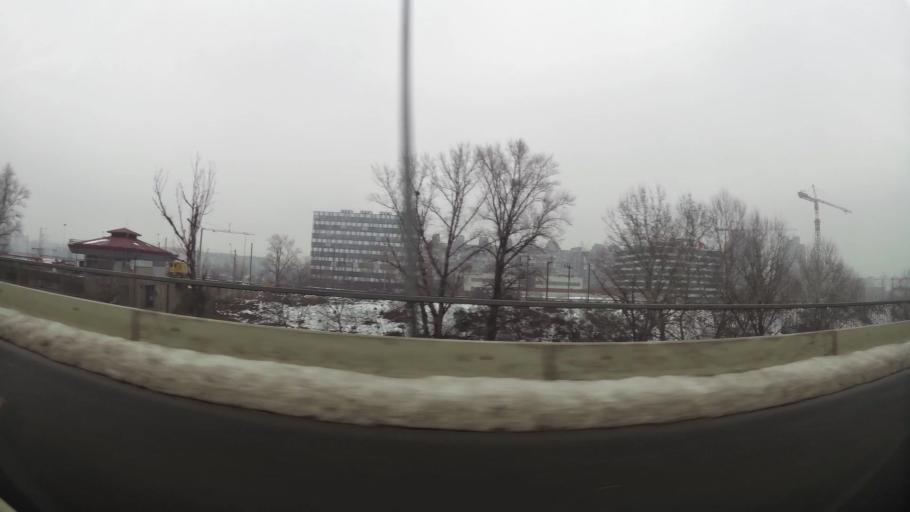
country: RS
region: Central Serbia
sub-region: Belgrade
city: Novi Beograd
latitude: 44.8057
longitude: 20.4188
